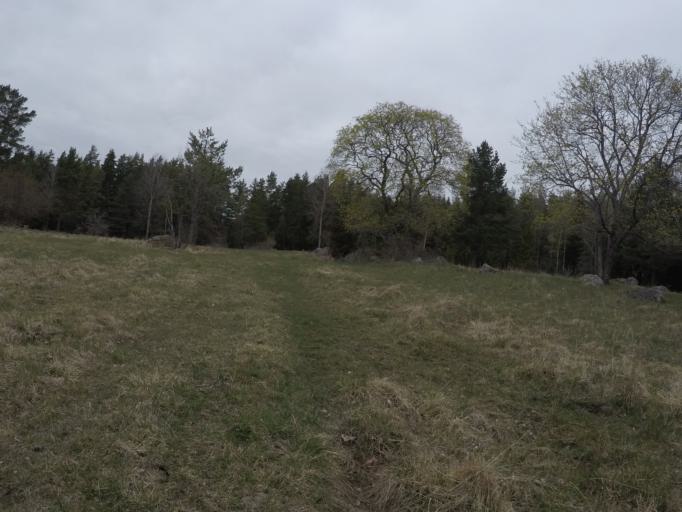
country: SE
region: Soedermanland
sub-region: Eskilstuna Kommun
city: Kvicksund
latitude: 59.3942
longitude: 16.2603
